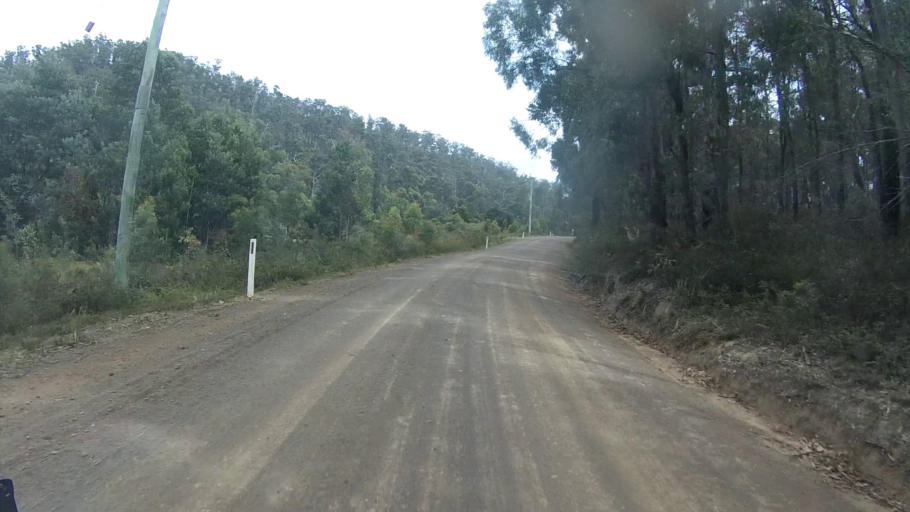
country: AU
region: Tasmania
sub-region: Sorell
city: Sorell
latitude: -42.7653
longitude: 147.8040
